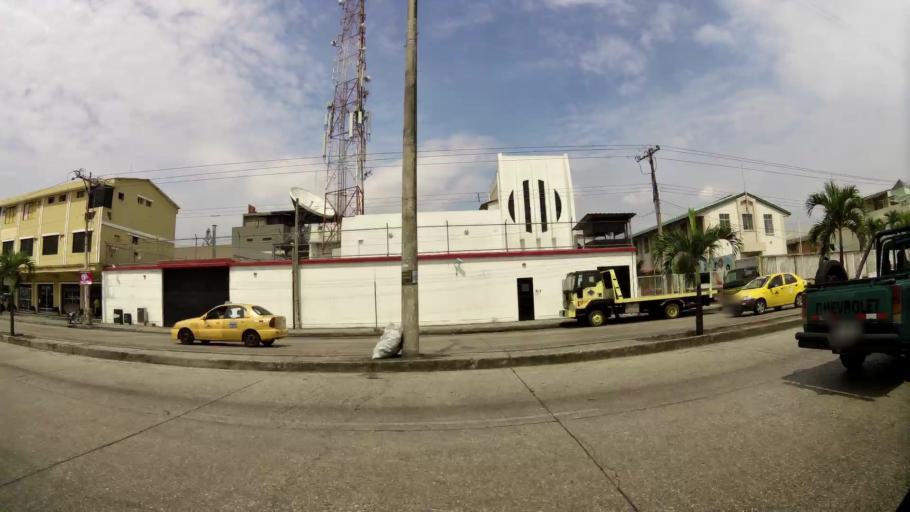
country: EC
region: Guayas
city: Eloy Alfaro
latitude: -2.1462
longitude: -79.8986
